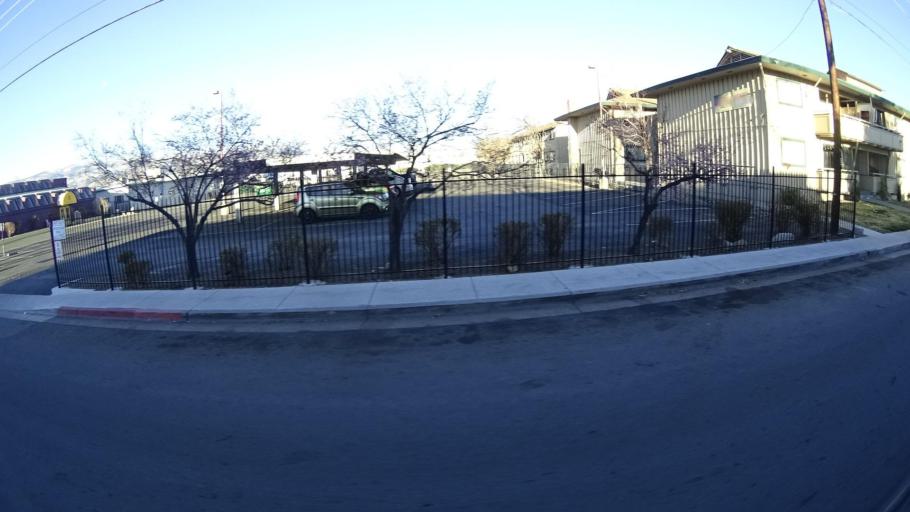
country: US
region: Nevada
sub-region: Washoe County
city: Reno
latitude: 39.5137
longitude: -119.7857
